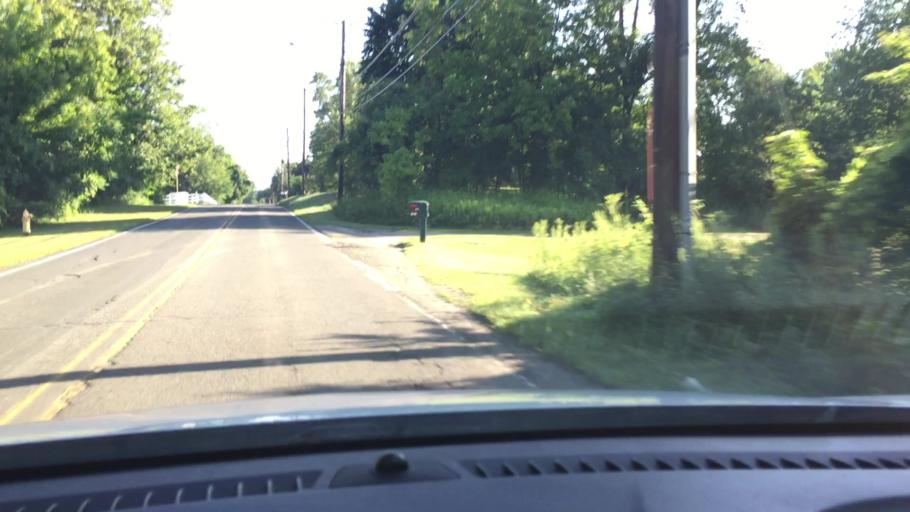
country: US
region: Massachusetts
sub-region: Berkshire County
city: Pittsfield
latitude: 42.4206
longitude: -73.2253
